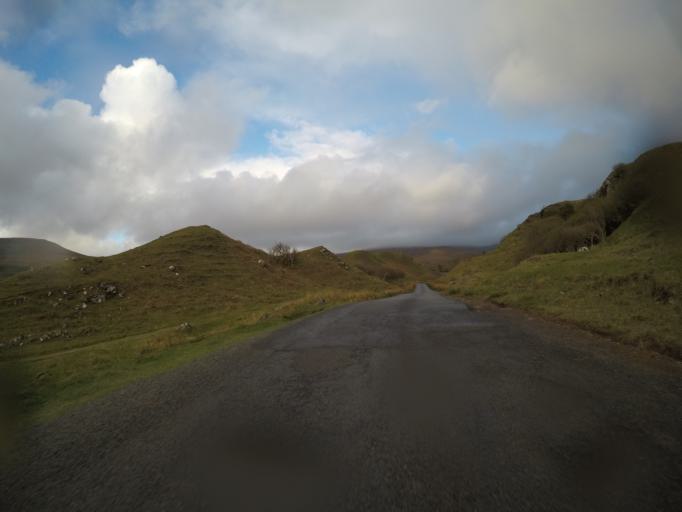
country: GB
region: Scotland
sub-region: Highland
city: Portree
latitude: 57.5840
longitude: -6.3289
